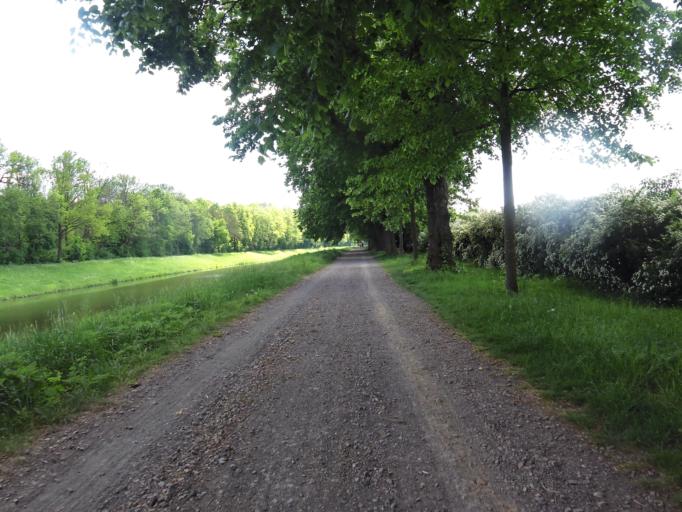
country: DE
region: Saxony
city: Leipzig
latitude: 51.3138
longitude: 12.3495
